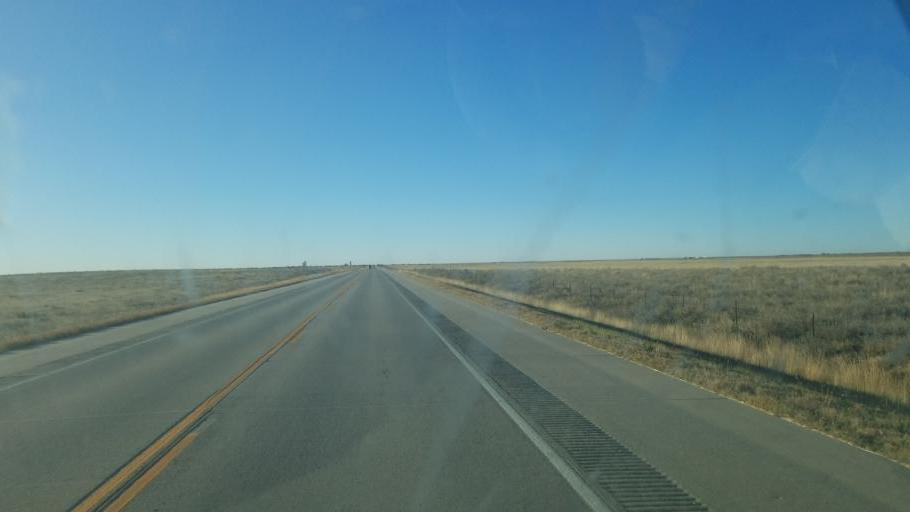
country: US
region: Colorado
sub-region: Kiowa County
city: Eads
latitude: 38.5250
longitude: -102.7858
